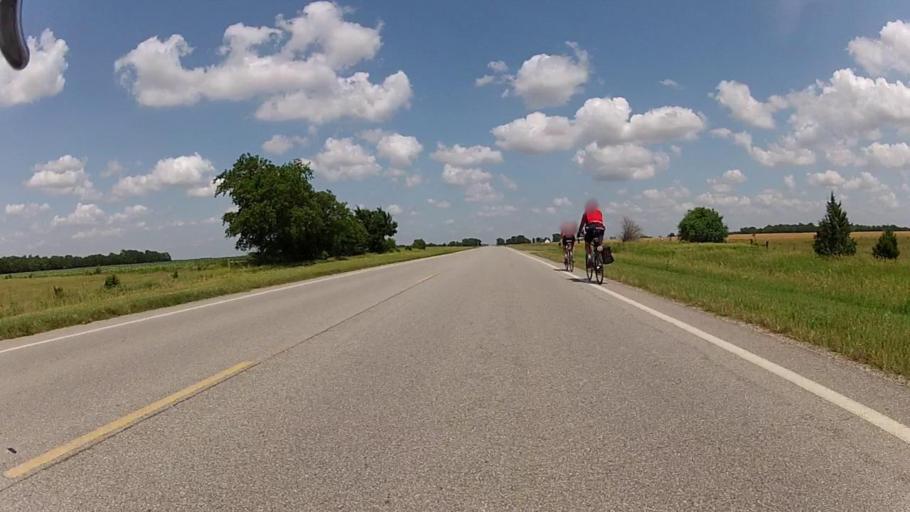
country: US
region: Kansas
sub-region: Labette County
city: Altamont
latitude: 37.1931
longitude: -95.2221
